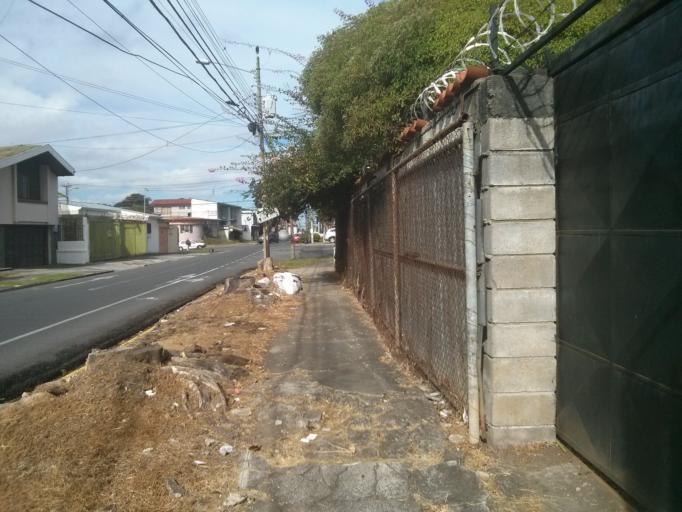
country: CR
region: San Jose
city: San Pedro
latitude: 9.9302
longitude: -84.0478
